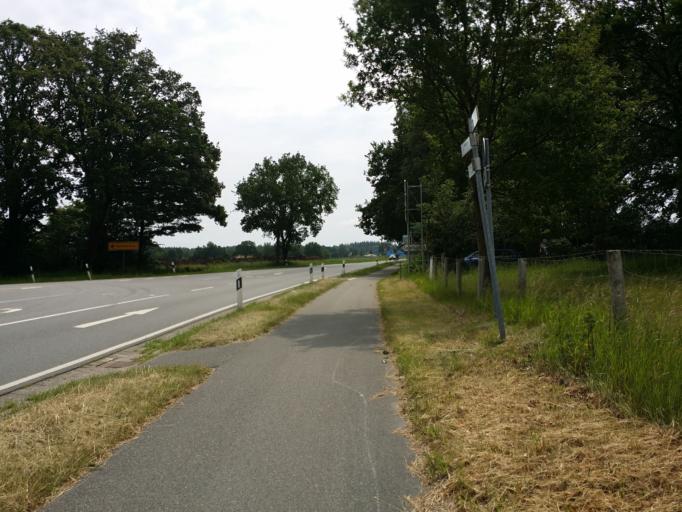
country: DE
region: Lower Saxony
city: Friedeburg
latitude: 53.4132
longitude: 7.8906
